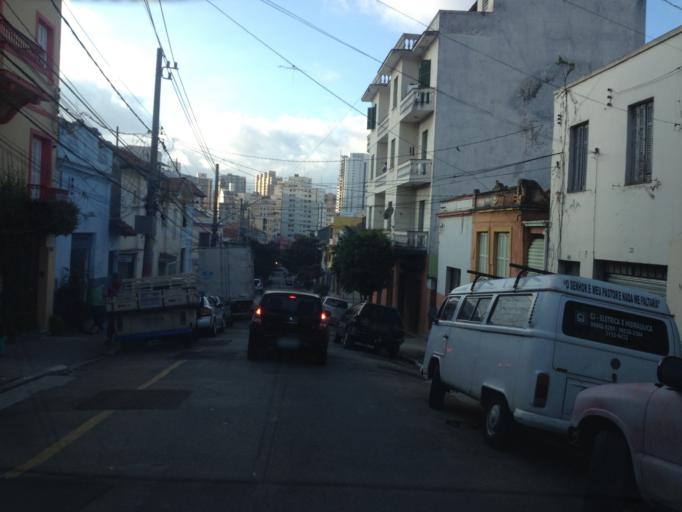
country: BR
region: Sao Paulo
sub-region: Sao Paulo
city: Sao Paulo
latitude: -23.5570
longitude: -46.6473
